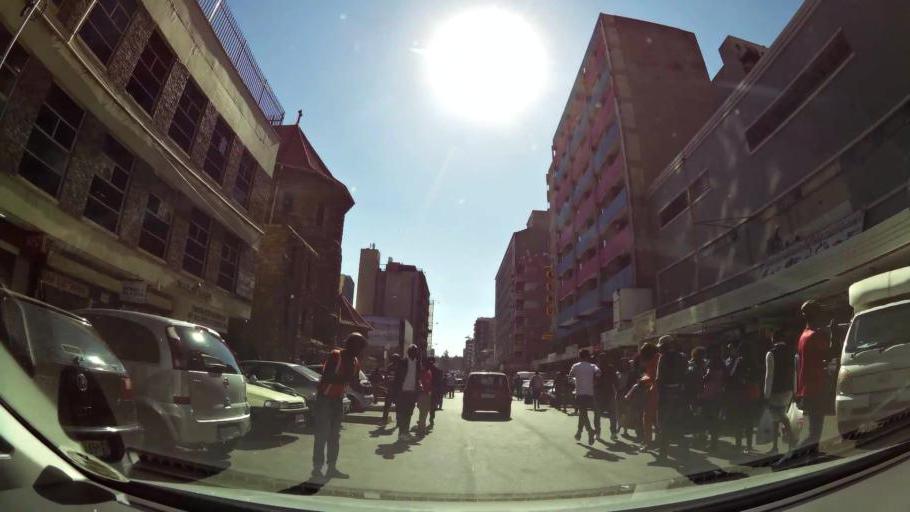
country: ZA
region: Gauteng
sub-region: City of Johannesburg Metropolitan Municipality
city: Johannesburg
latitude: -26.1997
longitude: 28.0449
